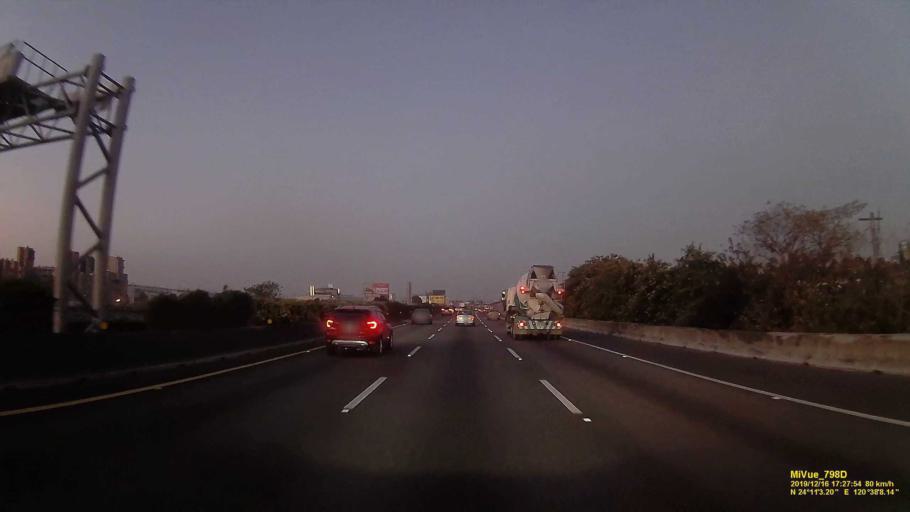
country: TW
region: Taiwan
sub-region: Taichung City
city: Taichung
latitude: 24.1867
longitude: 120.6366
